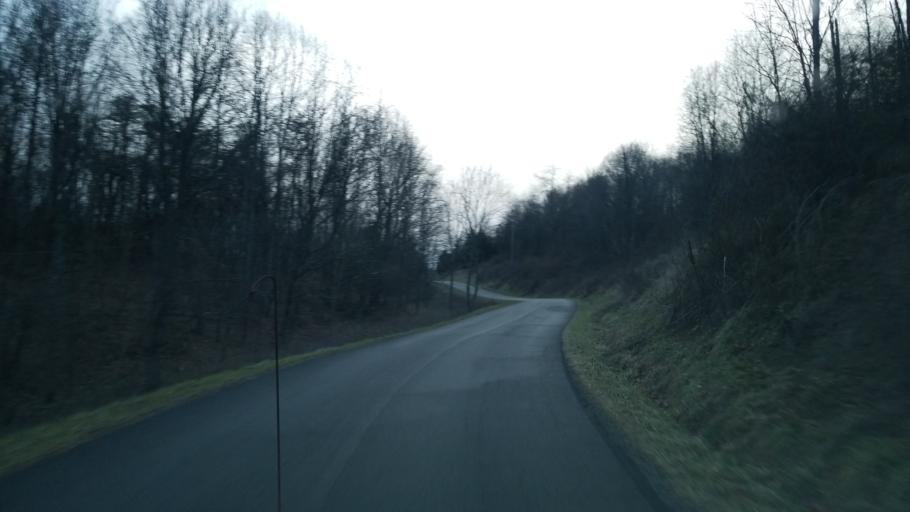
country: US
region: Virginia
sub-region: Pulaski County
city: Pulaski
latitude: 37.1480
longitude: -80.8746
